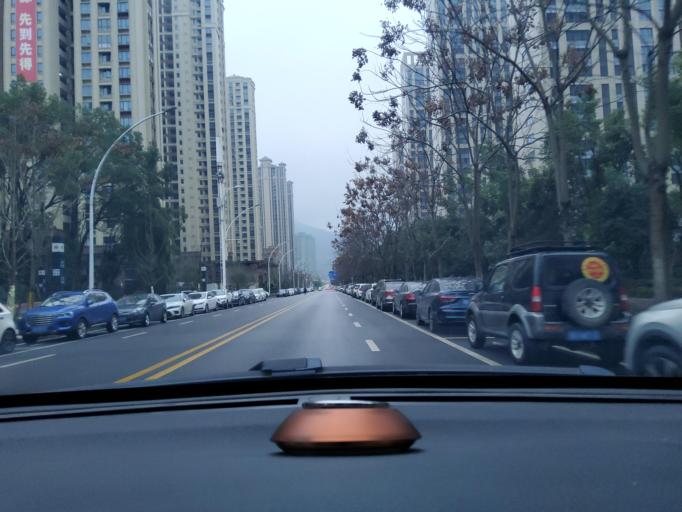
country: CN
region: Hubei
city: Tuanchengshan
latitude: 30.1985
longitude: 115.0094
